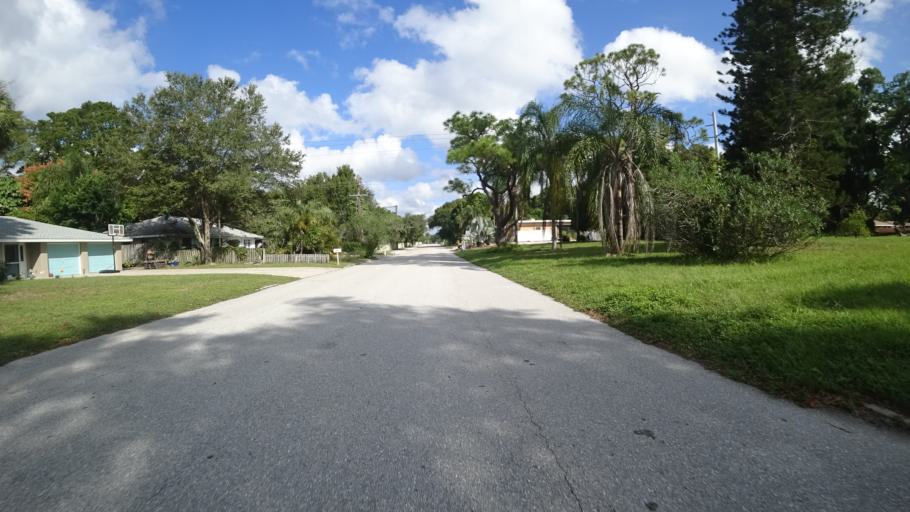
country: US
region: Florida
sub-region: Manatee County
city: West Bradenton
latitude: 27.4989
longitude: -82.6079
